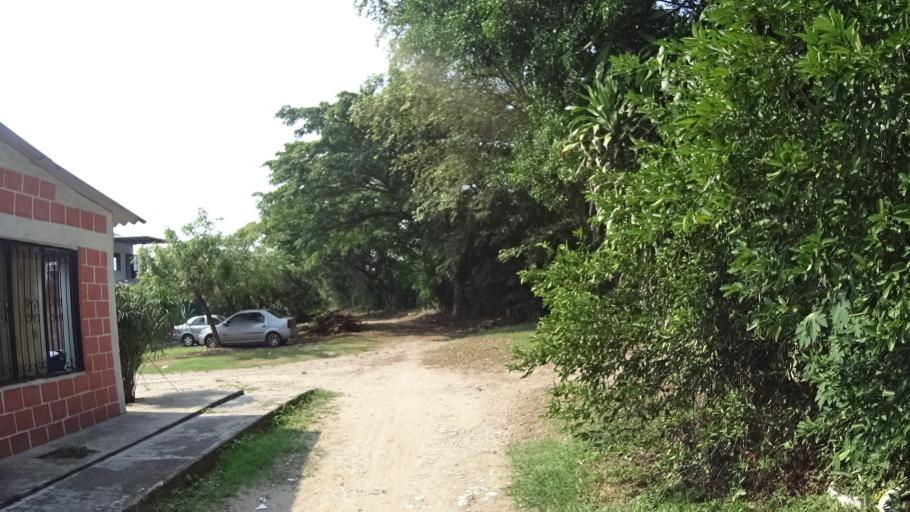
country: CO
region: Cundinamarca
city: Puerto Salgar
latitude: 5.4865
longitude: -74.6720
